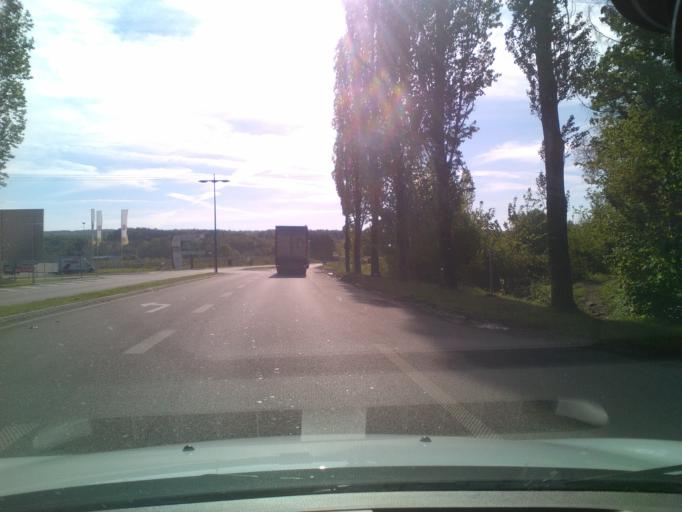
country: FR
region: Lorraine
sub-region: Departement des Vosges
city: Mirecourt
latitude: 48.3079
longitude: 6.1350
